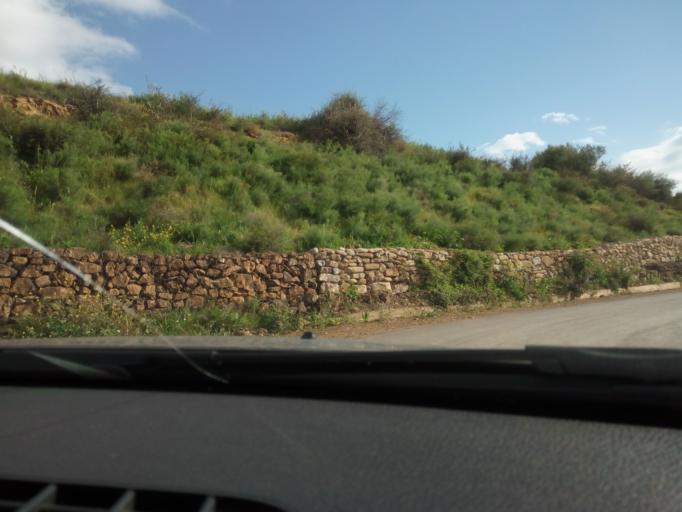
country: DZ
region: Tipaza
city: El Affroun
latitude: 36.3737
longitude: 2.5094
